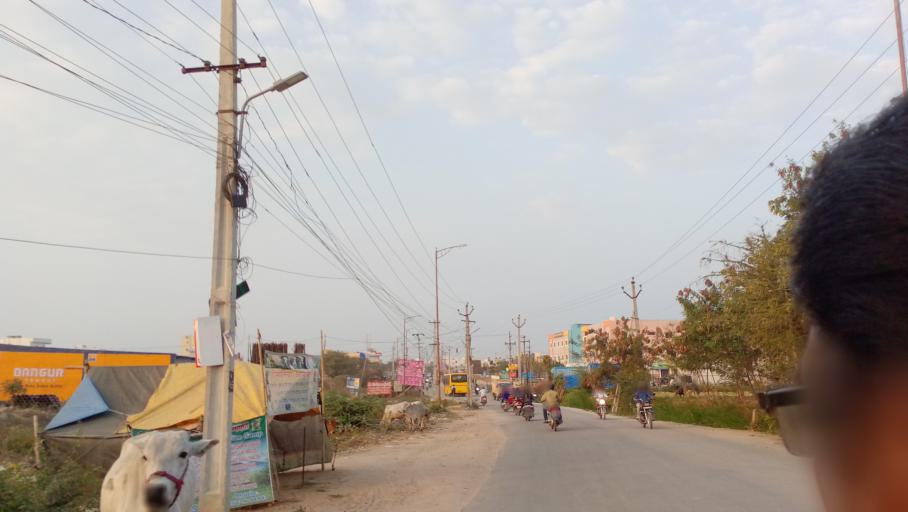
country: IN
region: Telangana
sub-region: Medak
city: Serilingampalle
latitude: 17.5143
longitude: 78.3189
